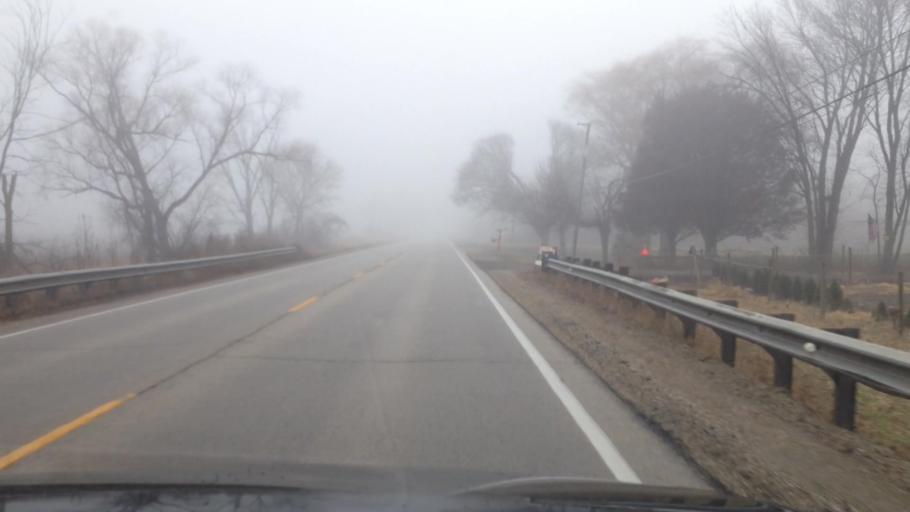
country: US
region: Illinois
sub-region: McHenry County
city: Woodstock
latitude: 42.3720
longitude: -88.4431
